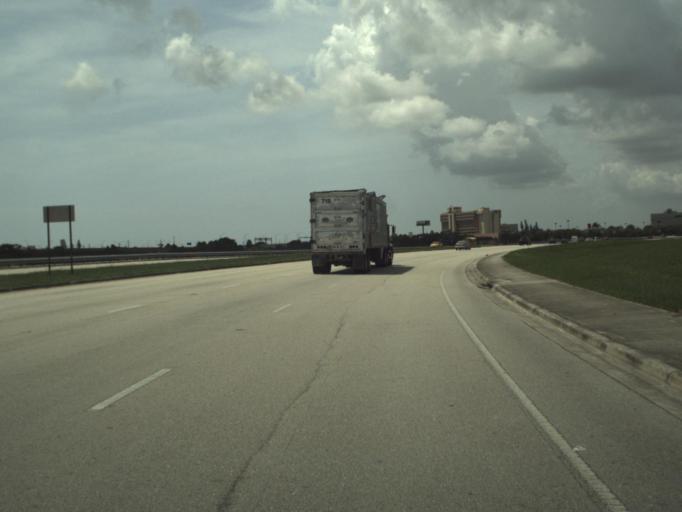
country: US
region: Florida
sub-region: Palm Beach County
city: West Palm Beach
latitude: 26.6856
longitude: -80.0740
